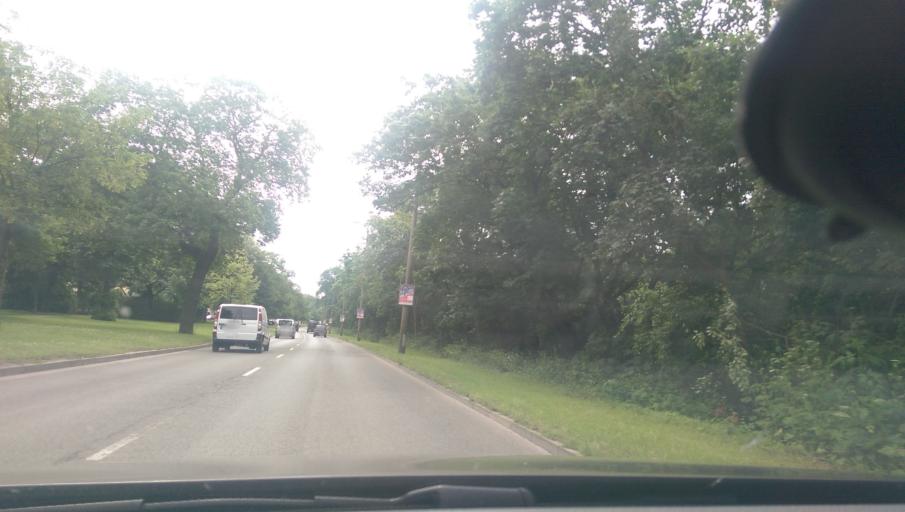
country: DE
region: Thuringia
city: Erfurt
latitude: 50.9835
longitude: 11.0350
